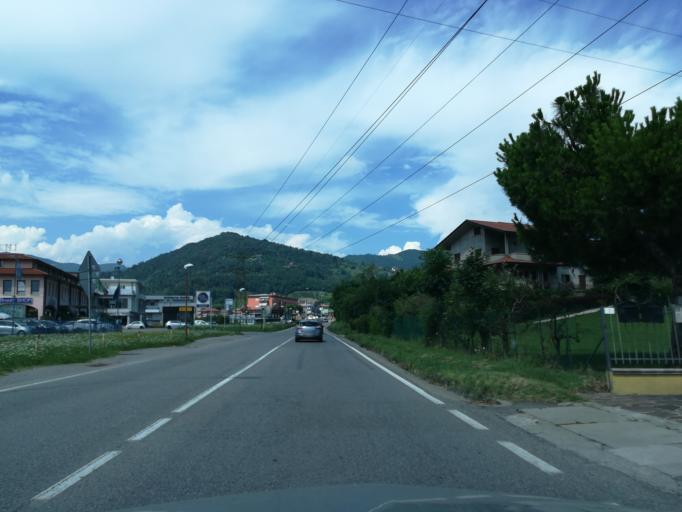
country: IT
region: Lombardy
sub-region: Provincia di Bergamo
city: Alme
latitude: 45.7434
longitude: 9.6113
